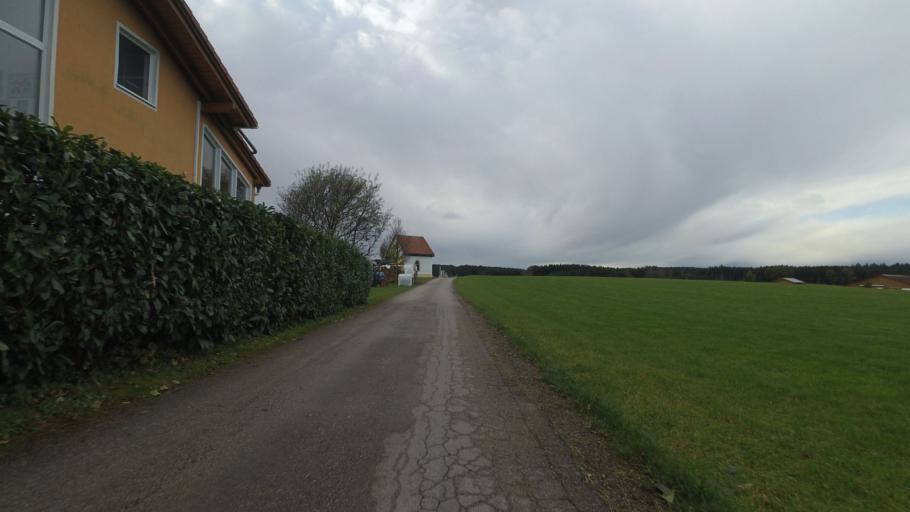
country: DE
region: Bavaria
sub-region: Upper Bavaria
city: Nussdorf
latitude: 47.9092
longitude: 12.5904
